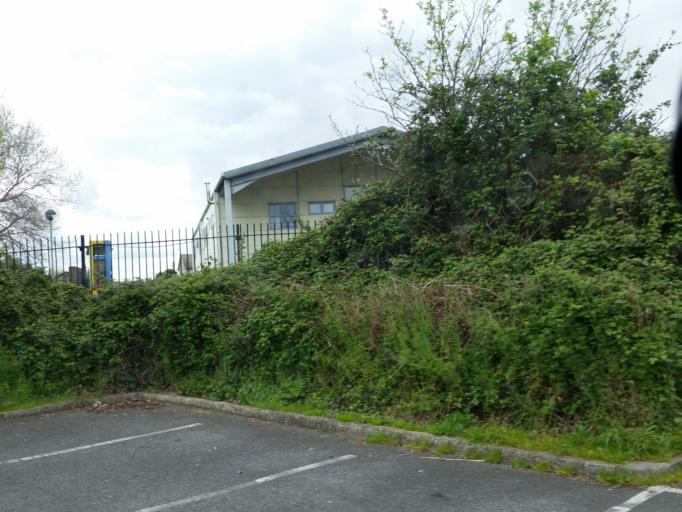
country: IE
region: Leinster
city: Beaumont
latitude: 53.3965
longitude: -6.2299
